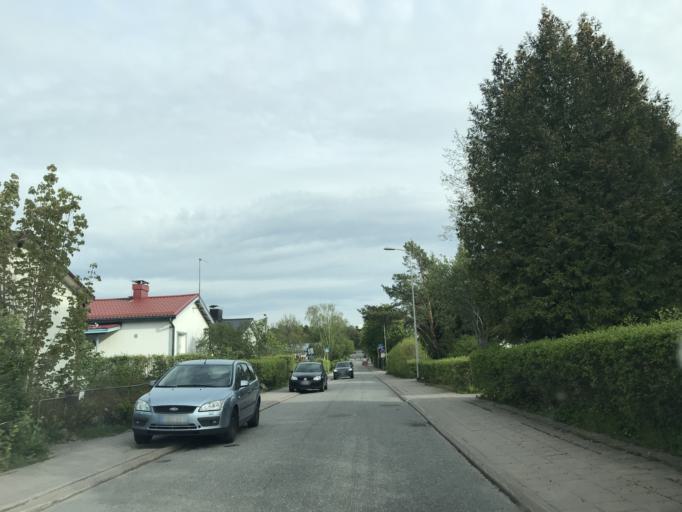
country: FI
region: Varsinais-Suomi
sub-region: Turku
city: Turku
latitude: 60.4401
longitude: 22.2973
